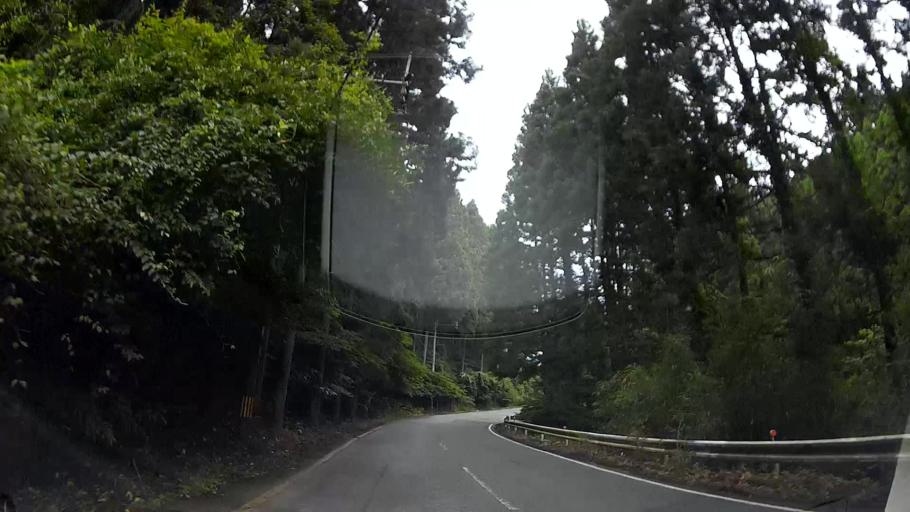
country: JP
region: Kumamoto
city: Kikuchi
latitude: 33.0252
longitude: 130.8939
